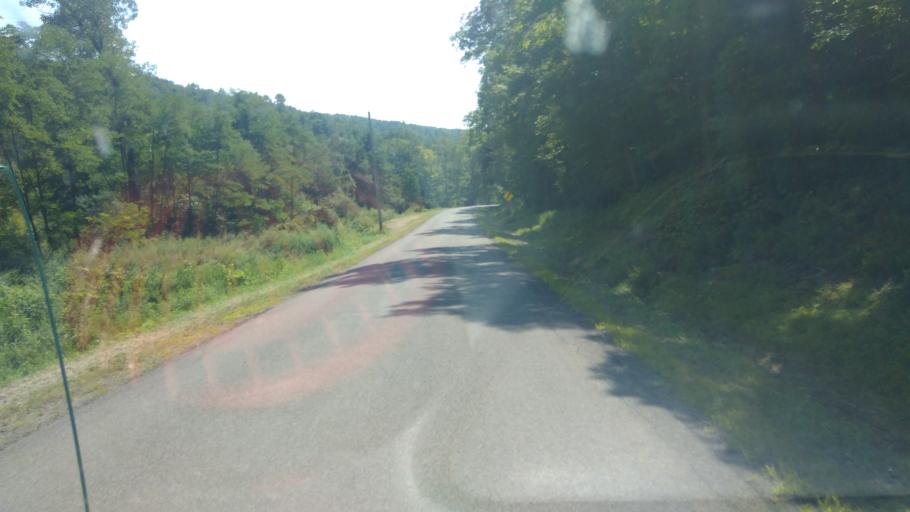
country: US
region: New York
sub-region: Steuben County
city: Canisteo
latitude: 42.3094
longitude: -77.6073
